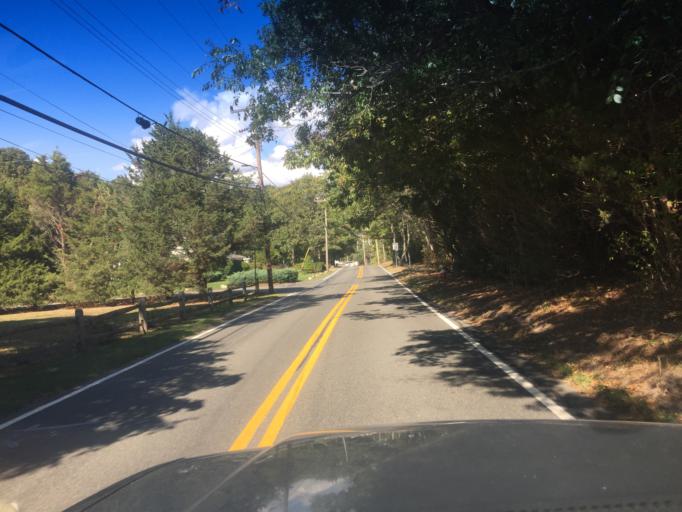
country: US
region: Massachusetts
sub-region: Barnstable County
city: Pocasset
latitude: 41.6827
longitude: -70.6143
